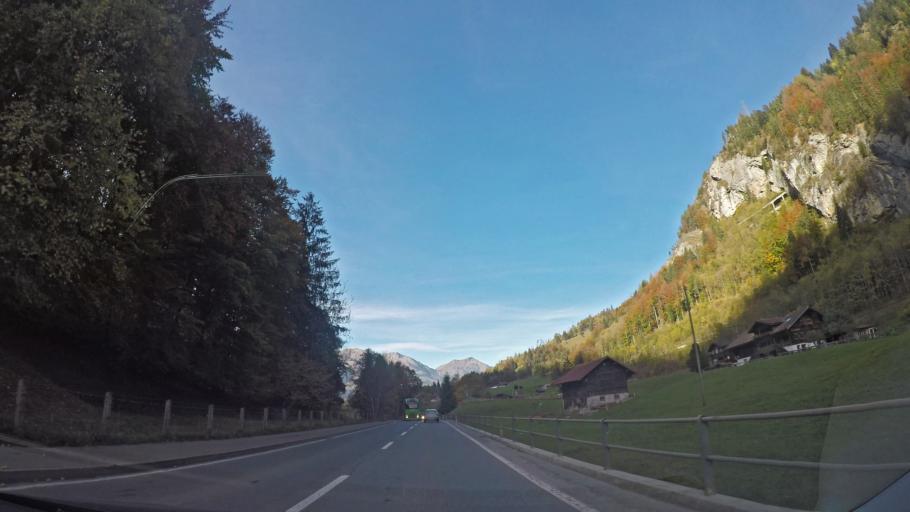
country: CH
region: Bern
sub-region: Frutigen-Niedersimmental District
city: Kandersteg
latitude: 46.5408
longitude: 7.6670
